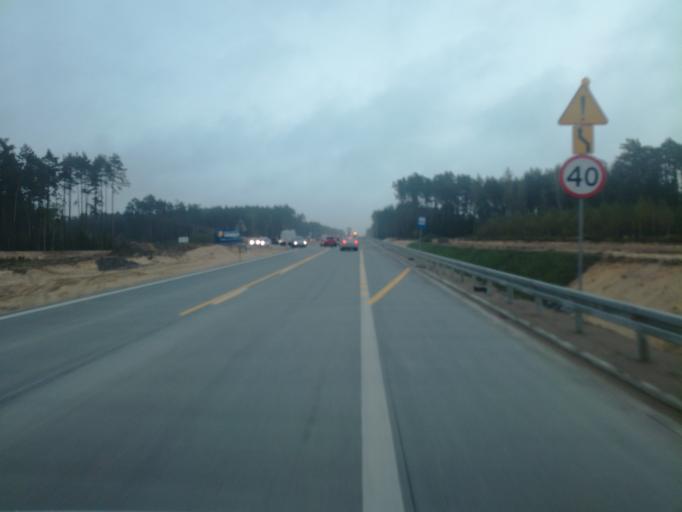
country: PL
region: Masovian Voivodeship
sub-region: Powiat ostrowski
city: Brok
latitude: 52.7363
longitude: 21.7480
